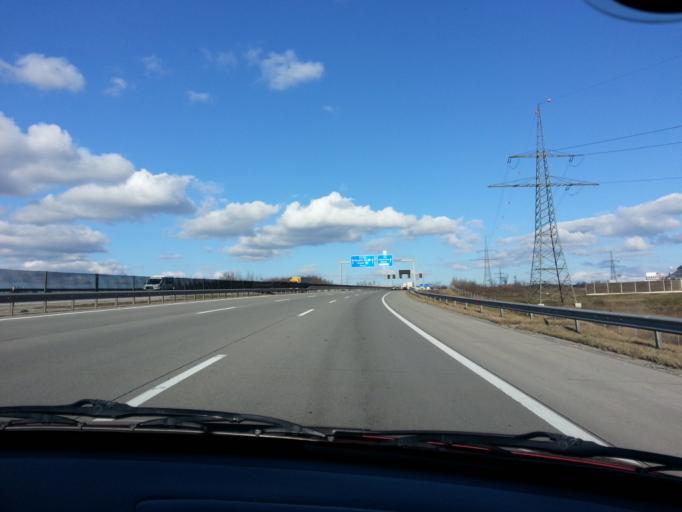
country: HU
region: Pest
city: Ecser
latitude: 47.4583
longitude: 19.3294
